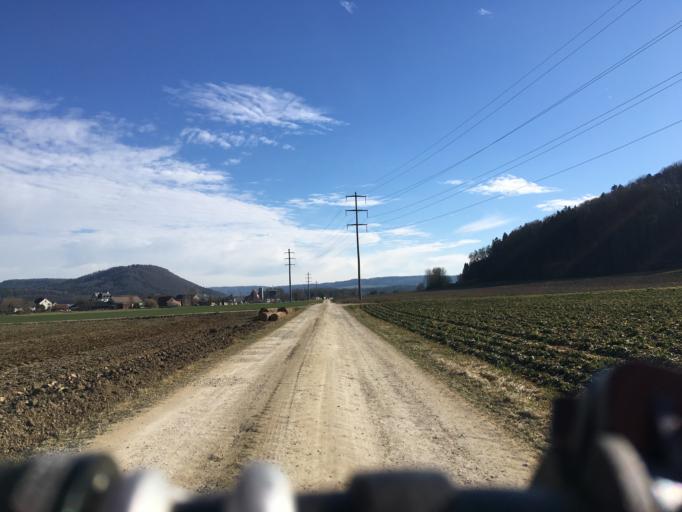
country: CH
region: Schaffhausen
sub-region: Bezirk Stein
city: Ramsen
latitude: 47.7009
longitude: 8.8084
